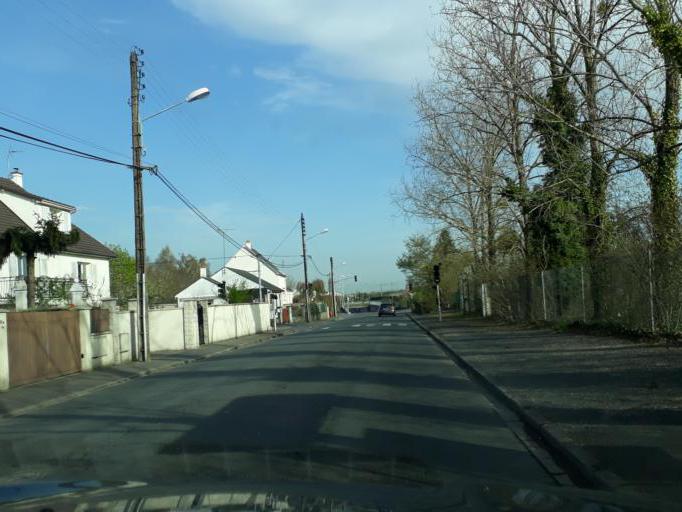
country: FR
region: Centre
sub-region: Departement du Loiret
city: La Chapelle-Saint-Mesmin
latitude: 47.8947
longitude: 1.8385
